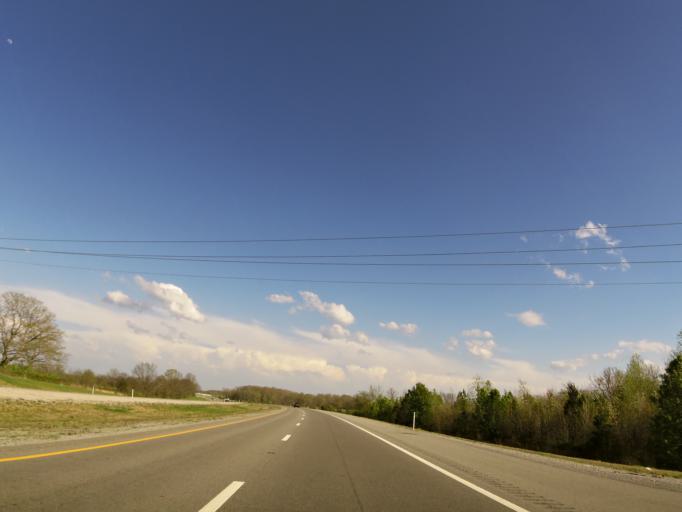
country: US
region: Tennessee
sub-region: Williamson County
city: Fairview
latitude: 35.9118
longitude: -87.1634
